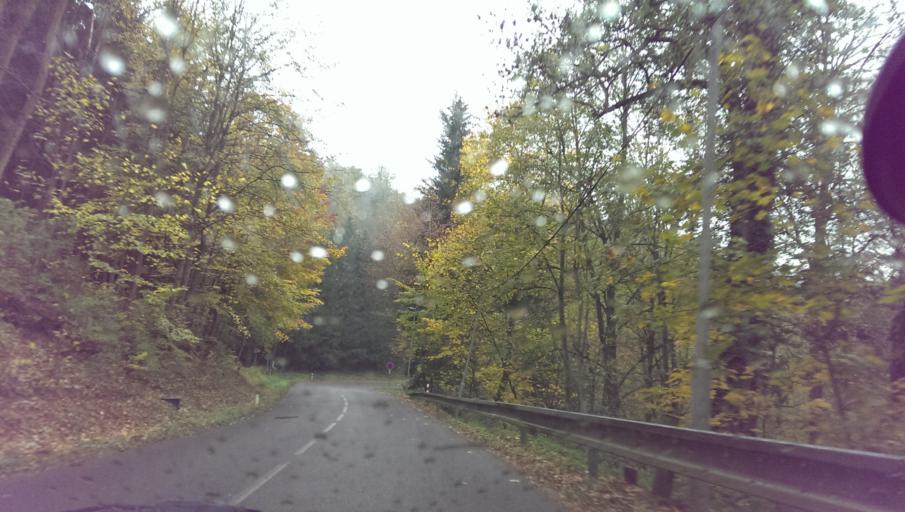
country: AT
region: Lower Austria
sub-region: Politischer Bezirk Hollabrunn
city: Hardegg
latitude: 48.8939
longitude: 15.8077
